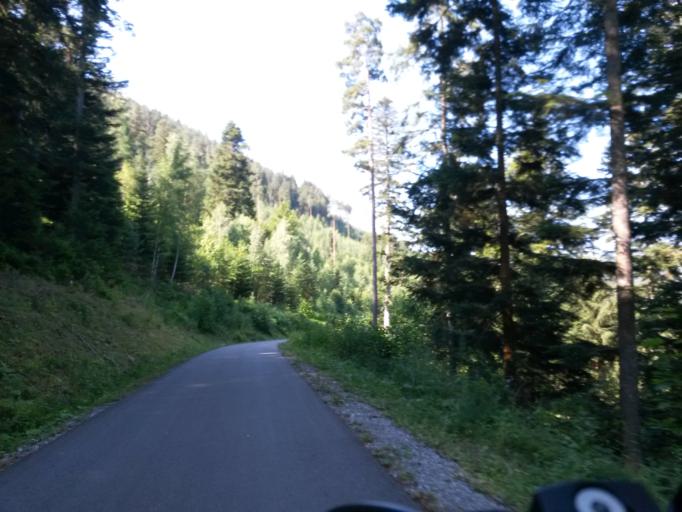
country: DE
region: Baden-Wuerttemberg
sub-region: Karlsruhe Region
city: Enzklosterle
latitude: 48.6942
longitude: 8.5127
